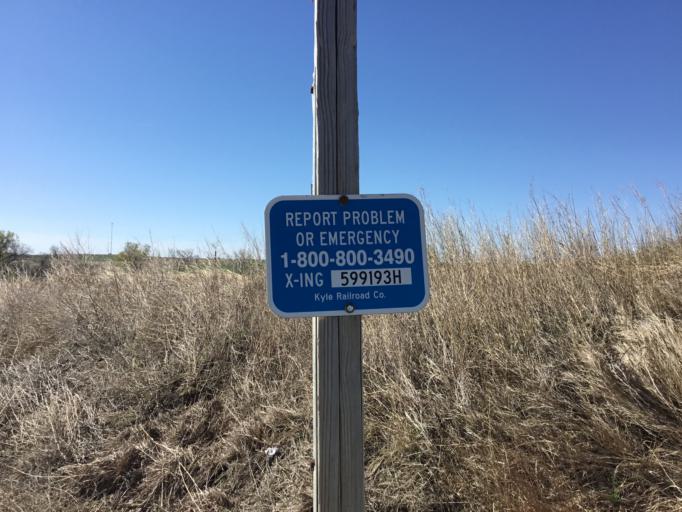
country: US
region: Kansas
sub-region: Phillips County
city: Phillipsburg
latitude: 39.8428
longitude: -99.6007
